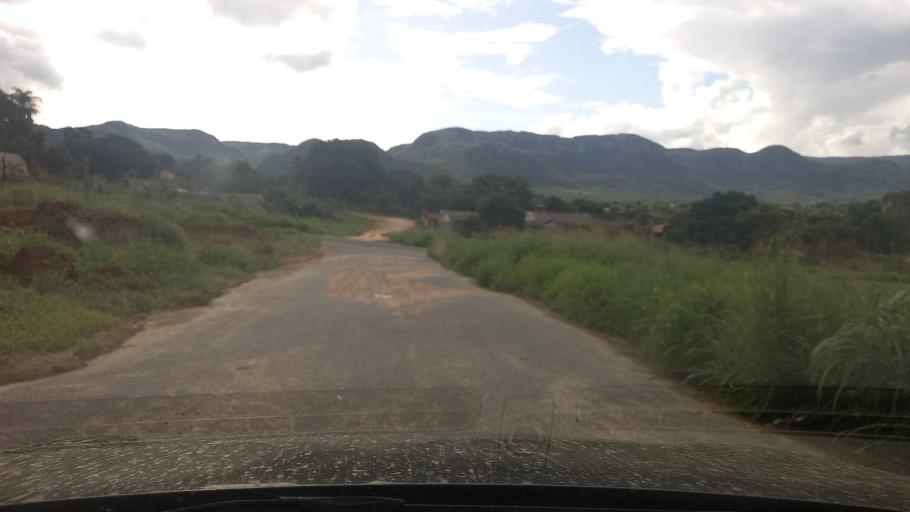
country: BR
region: Goias
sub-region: Cavalcante
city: Cavalcante
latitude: -13.7973
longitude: -47.4483
